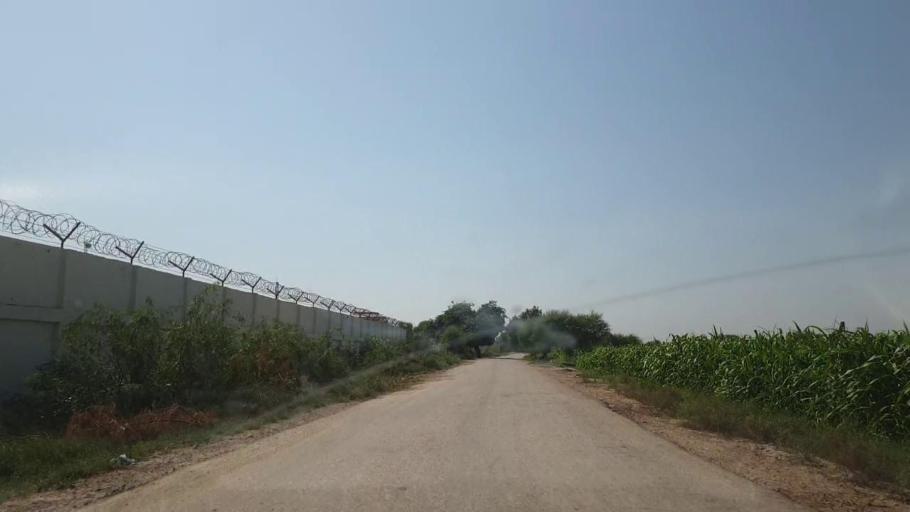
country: PK
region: Sindh
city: Tando Jam
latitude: 25.3889
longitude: 68.5818
